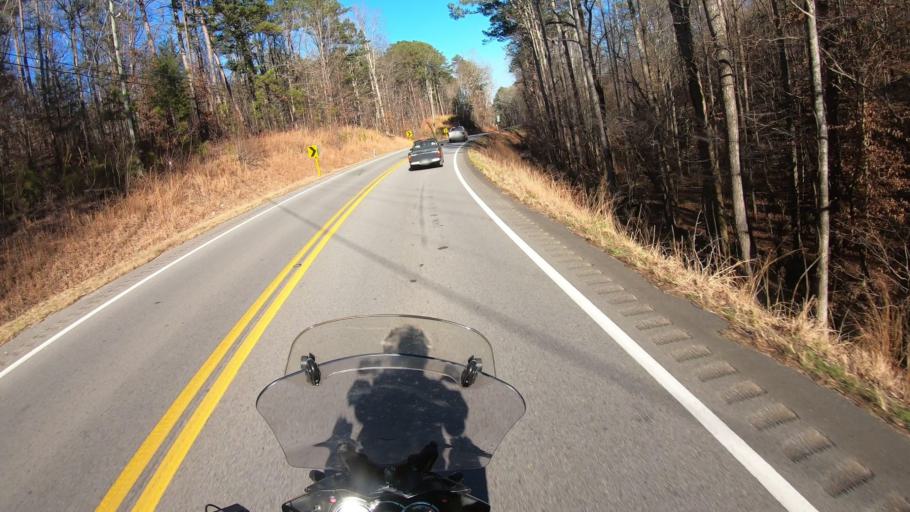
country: US
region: Alabama
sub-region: Cleburne County
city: Heflin
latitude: 33.6948
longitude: -85.5236
